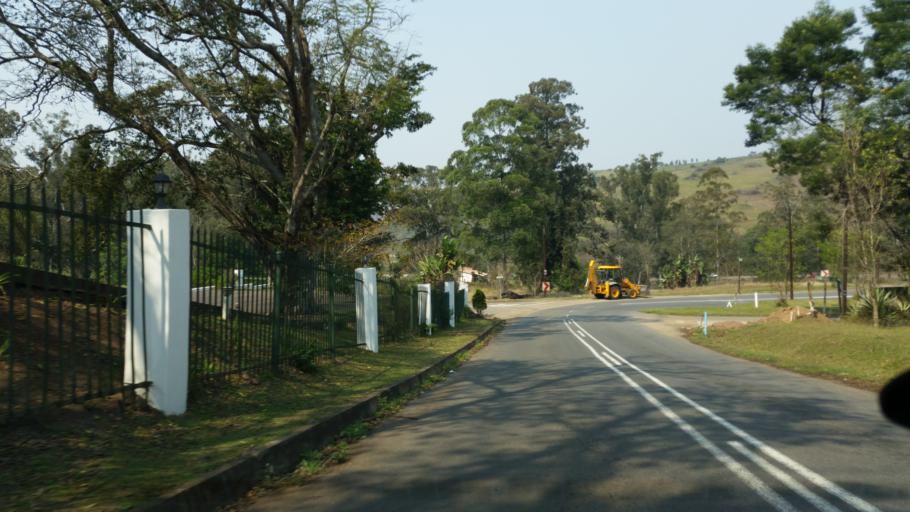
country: ZA
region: KwaZulu-Natal
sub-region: eThekwini Metropolitan Municipality
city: Mpumalanga
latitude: -29.7396
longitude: 30.6634
